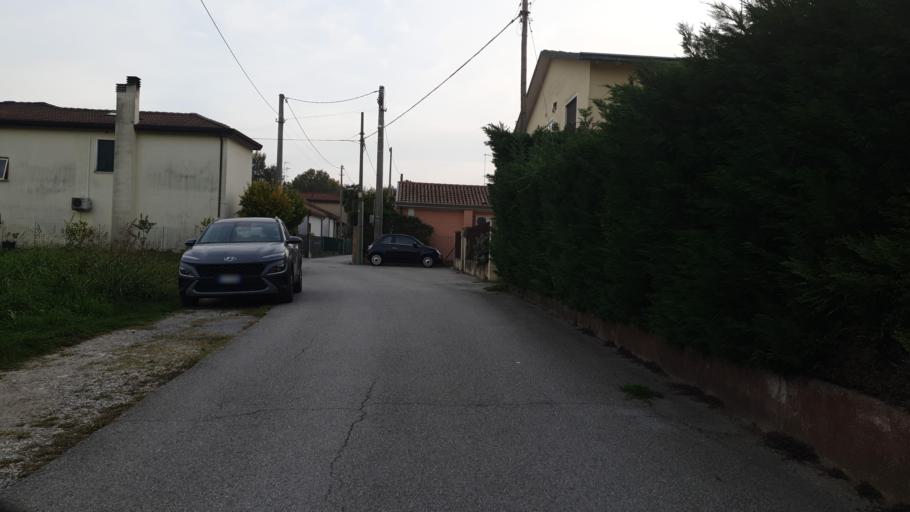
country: IT
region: Veneto
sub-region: Provincia di Padova
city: Noventa
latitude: 45.4021
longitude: 11.9482
